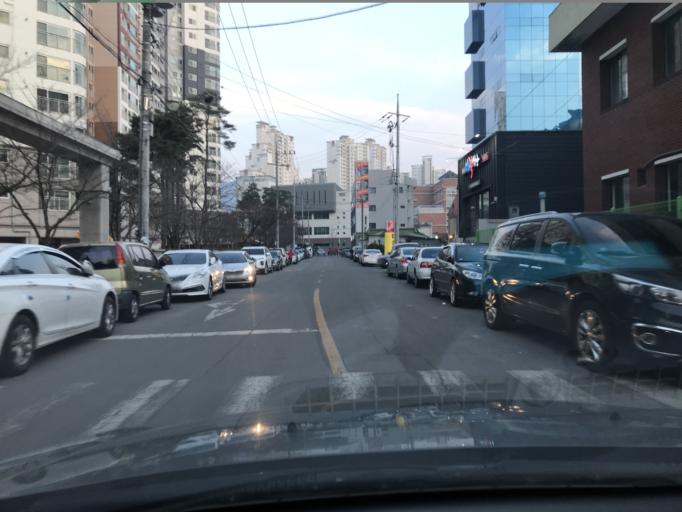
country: KR
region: Daegu
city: Hwawon
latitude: 35.8185
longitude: 128.5173
